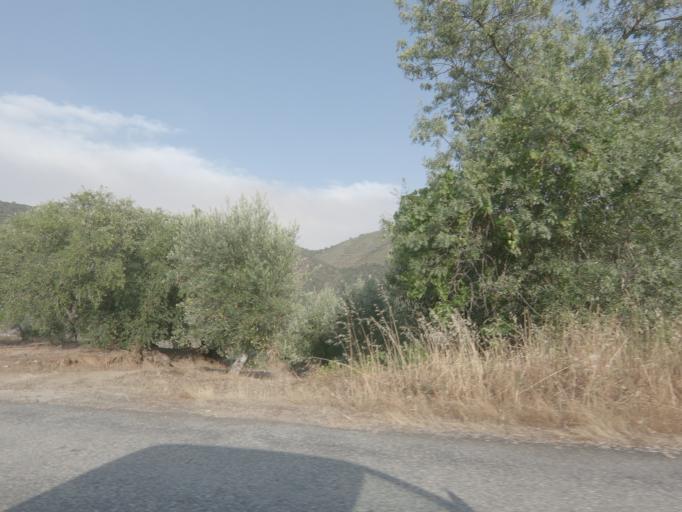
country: PT
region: Viseu
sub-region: Tabuaco
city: Tabuaco
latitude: 41.1228
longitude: -7.5497
